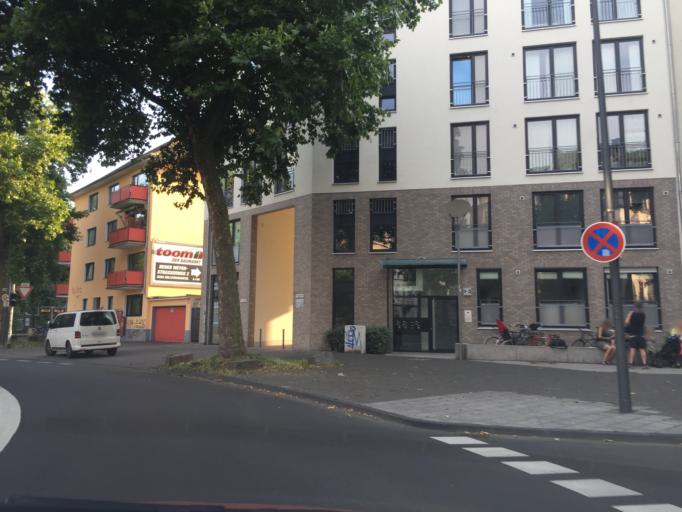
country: DE
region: North Rhine-Westphalia
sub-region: Regierungsbezirk Koln
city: Neustadt/Sued
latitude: 50.9242
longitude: 6.9440
